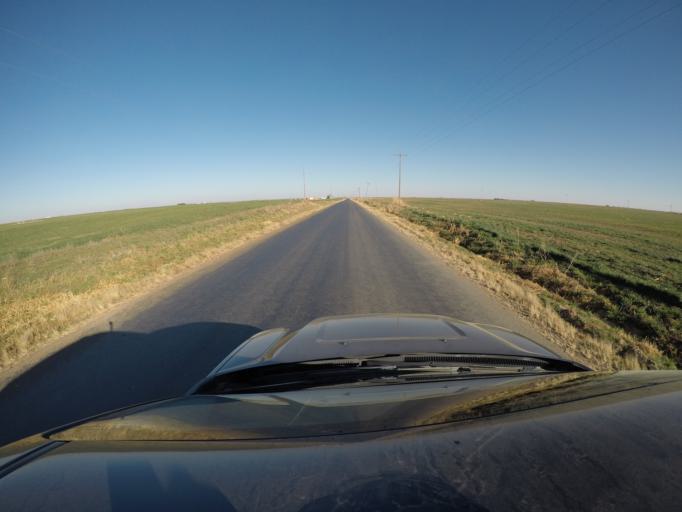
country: US
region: New Mexico
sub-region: Curry County
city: Texico
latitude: 34.3028
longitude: -103.1069
